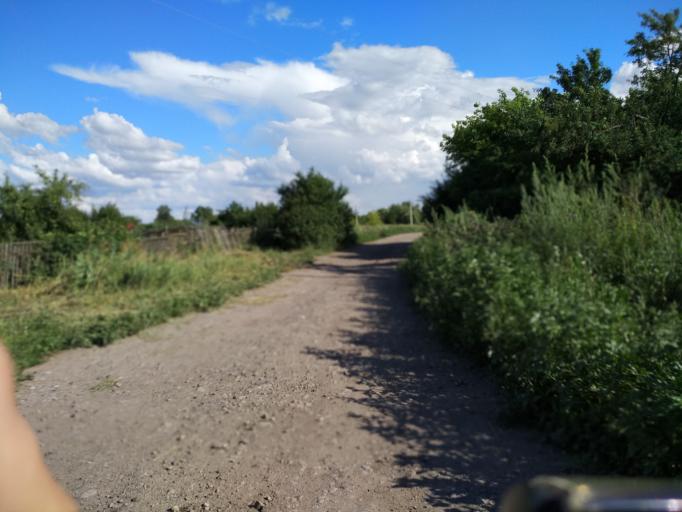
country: RU
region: Lipetsk
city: Dobrinka
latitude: 52.0331
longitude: 40.5625
